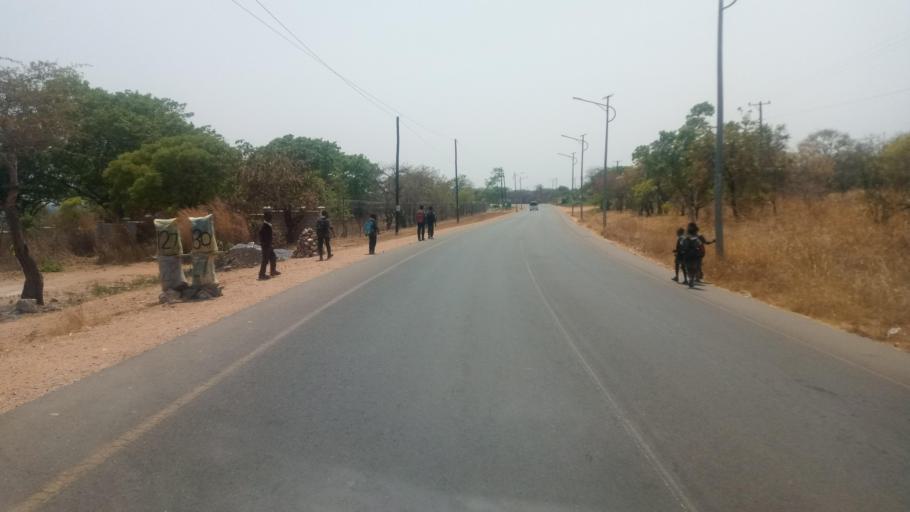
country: ZM
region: Lusaka
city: Lusaka
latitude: -15.4765
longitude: 28.4199
